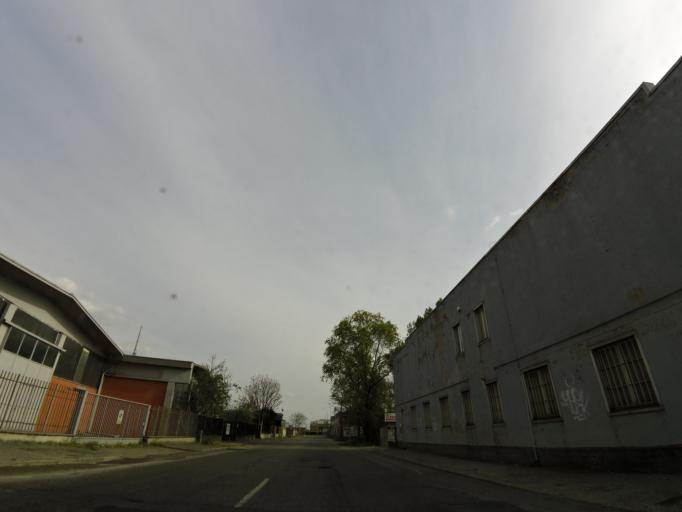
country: IT
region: Lombardy
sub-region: Citta metropolitana di Milano
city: Civesio
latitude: 45.3968
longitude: 9.2539
